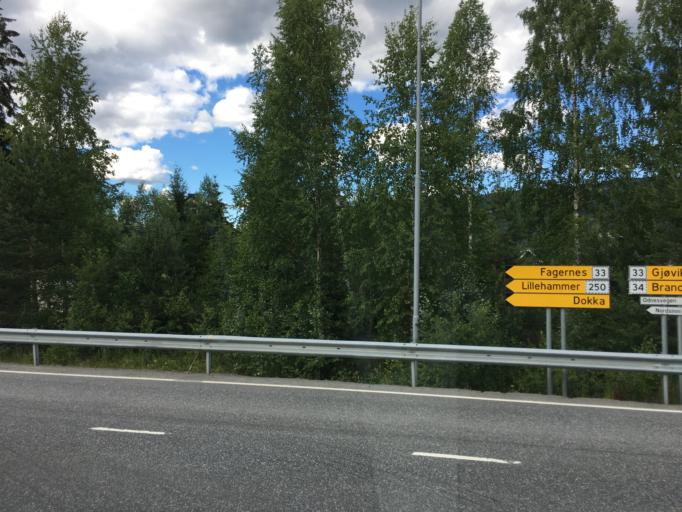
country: NO
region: Oppland
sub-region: Nordre Land
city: Dokka
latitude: 60.8285
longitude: 10.0693
